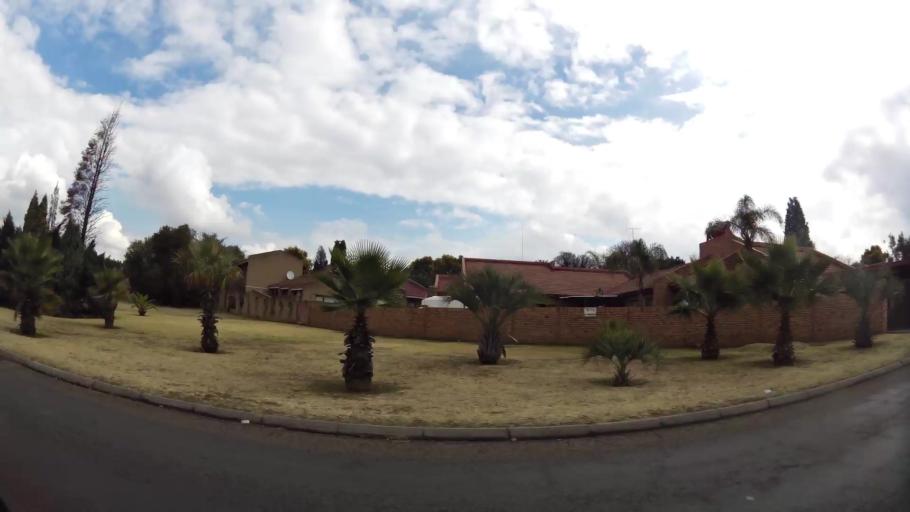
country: ZA
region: Gauteng
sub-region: Sedibeng District Municipality
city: Vanderbijlpark
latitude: -26.7427
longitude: 27.8545
